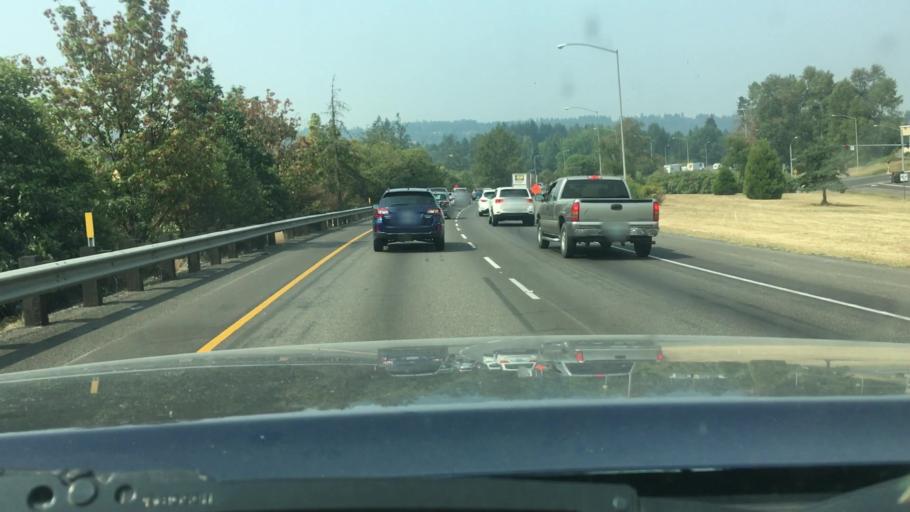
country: US
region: Oregon
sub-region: Clackamas County
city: West Linn
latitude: 45.3477
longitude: -122.6494
